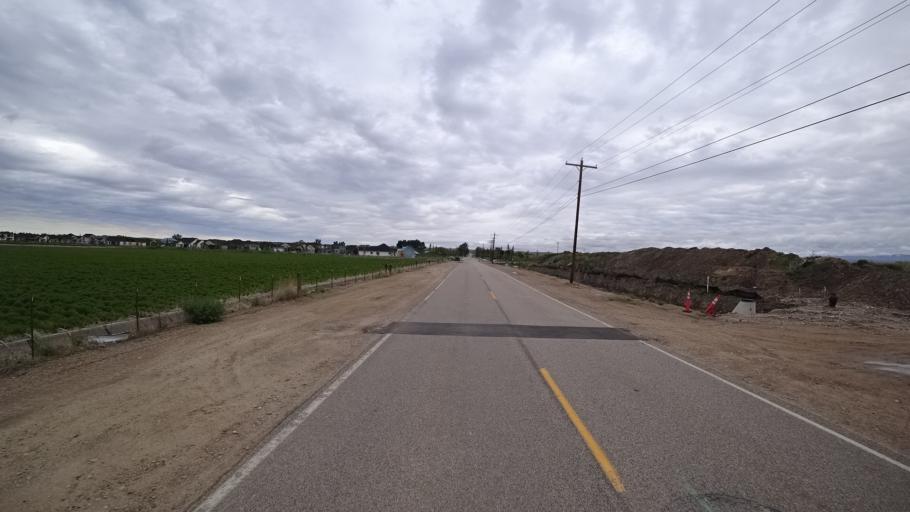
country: US
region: Idaho
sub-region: Ada County
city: Star
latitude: 43.7009
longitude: -116.4435
